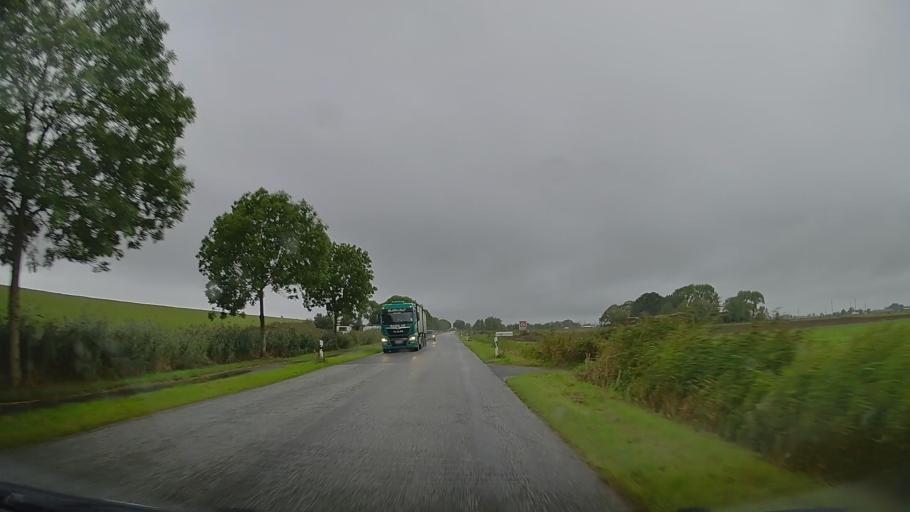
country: DE
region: Schleswig-Holstein
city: Sankt Margarethen
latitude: 53.8763
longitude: 9.2844
